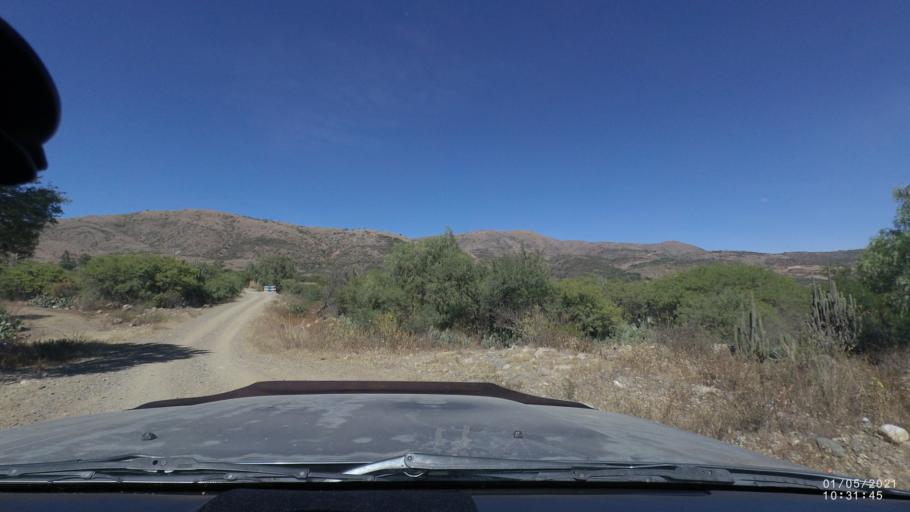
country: BO
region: Cochabamba
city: Capinota
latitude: -17.5927
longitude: -66.1960
